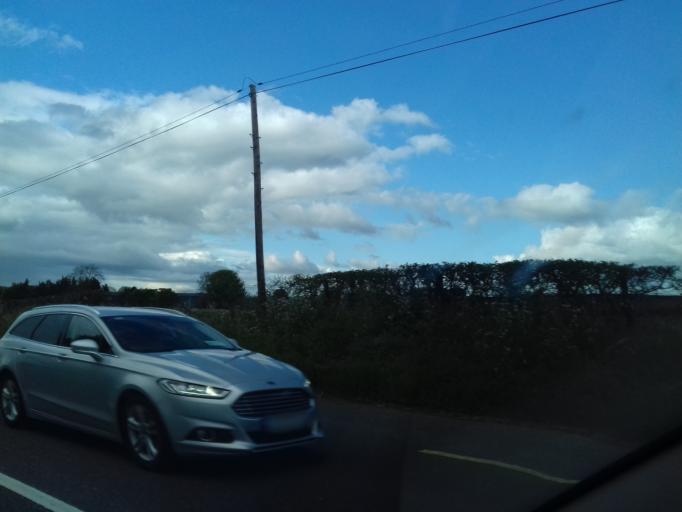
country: IE
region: Leinster
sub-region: Kilkenny
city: Kilkenny
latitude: 52.6146
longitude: -7.2464
